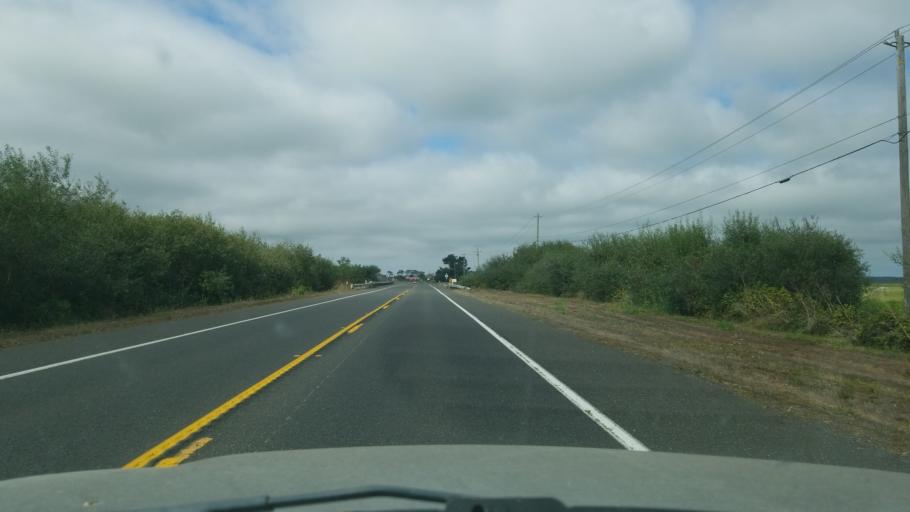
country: US
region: California
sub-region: Humboldt County
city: Ferndale
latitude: 40.5990
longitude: -124.2189
